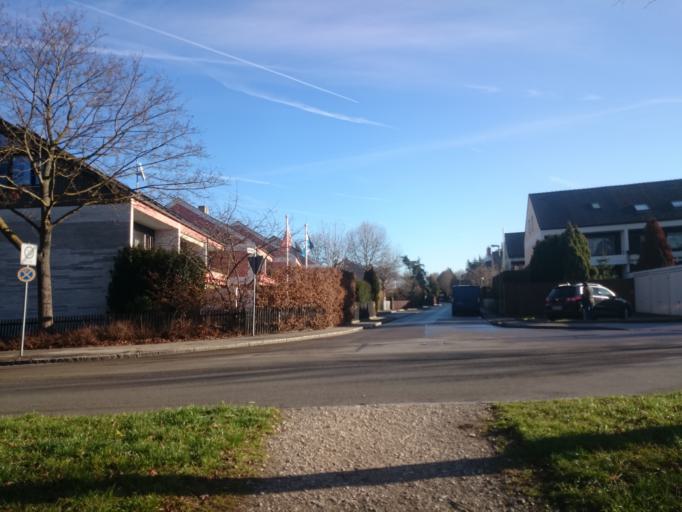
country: DE
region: Bavaria
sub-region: Swabia
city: Augsburg
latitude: 48.3265
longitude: 10.9043
